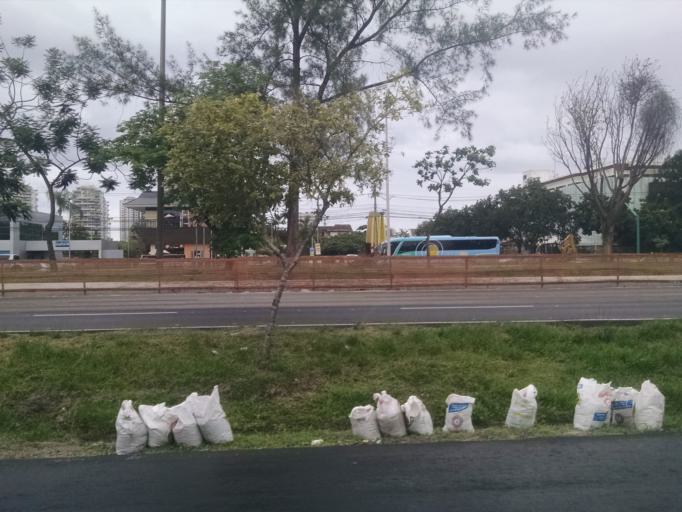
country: BR
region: Rio de Janeiro
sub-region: Rio De Janeiro
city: Rio de Janeiro
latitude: -23.0003
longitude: -43.3336
